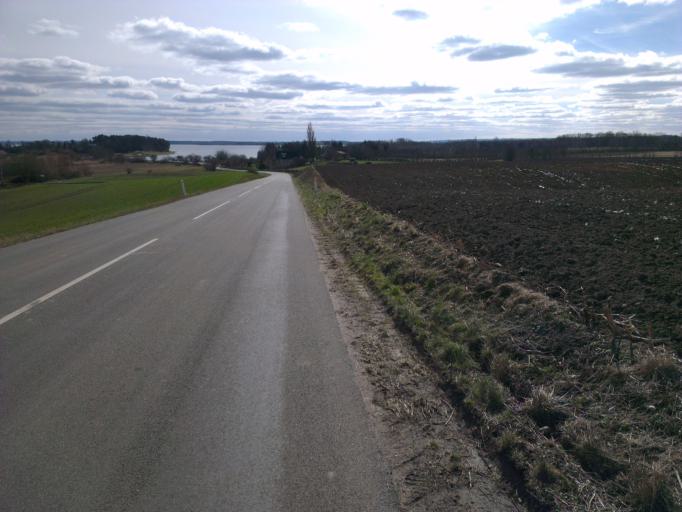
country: DK
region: Capital Region
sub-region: Frederikssund Kommune
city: Skibby
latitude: 55.7463
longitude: 11.9865
